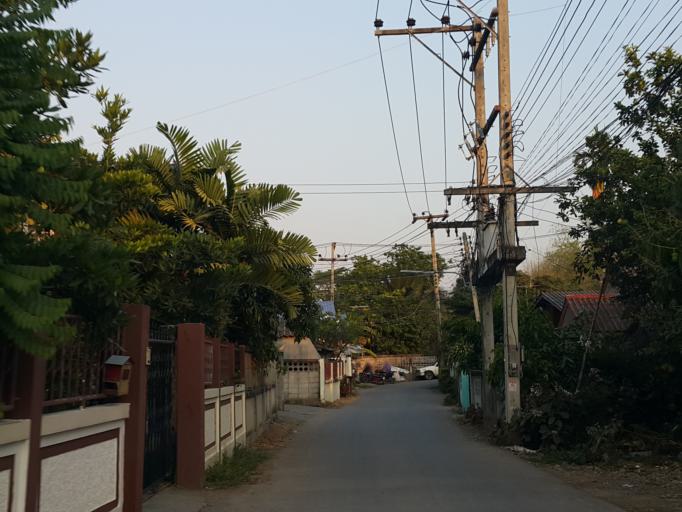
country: TH
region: Chiang Mai
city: San Sai
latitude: 18.8946
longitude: 98.9602
